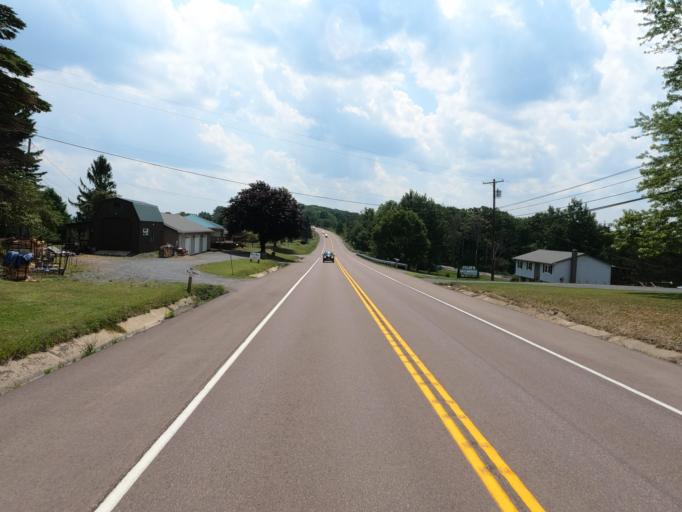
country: US
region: Maryland
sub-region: Garrett County
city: Mountain Lake Park
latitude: 39.4656
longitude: -79.3665
